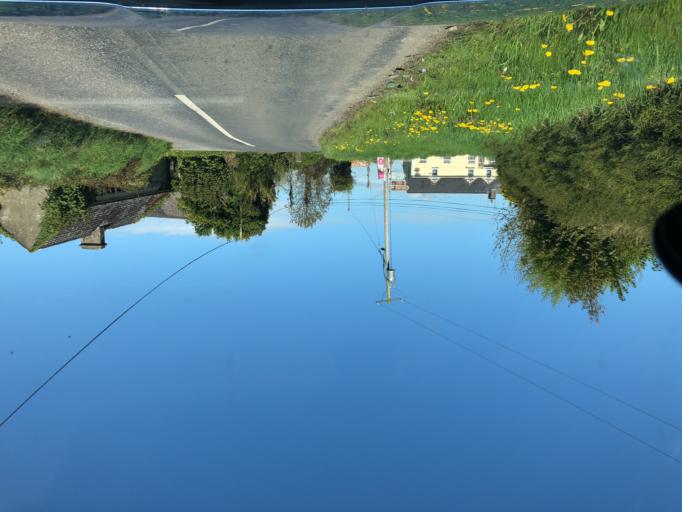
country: IE
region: Connaught
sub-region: County Galway
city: Portumna
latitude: 53.1567
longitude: -8.3871
